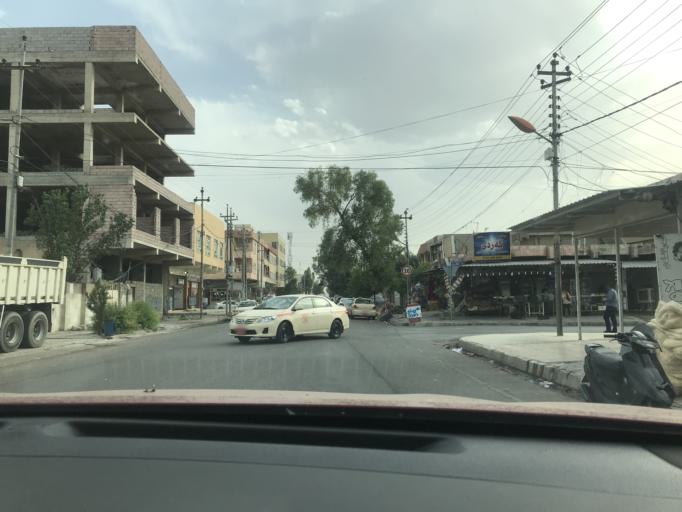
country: IQ
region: Arbil
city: Erbil
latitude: 36.1772
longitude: 43.9755
